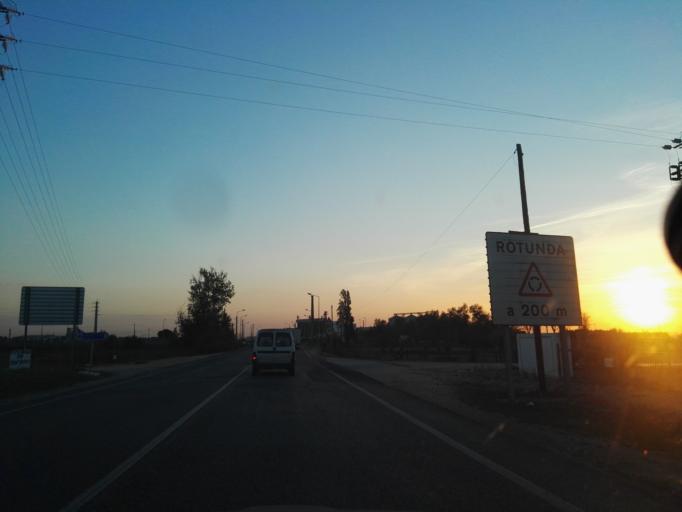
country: PT
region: Santarem
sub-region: Coruche
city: Coruche
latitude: 38.9489
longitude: -8.4981
